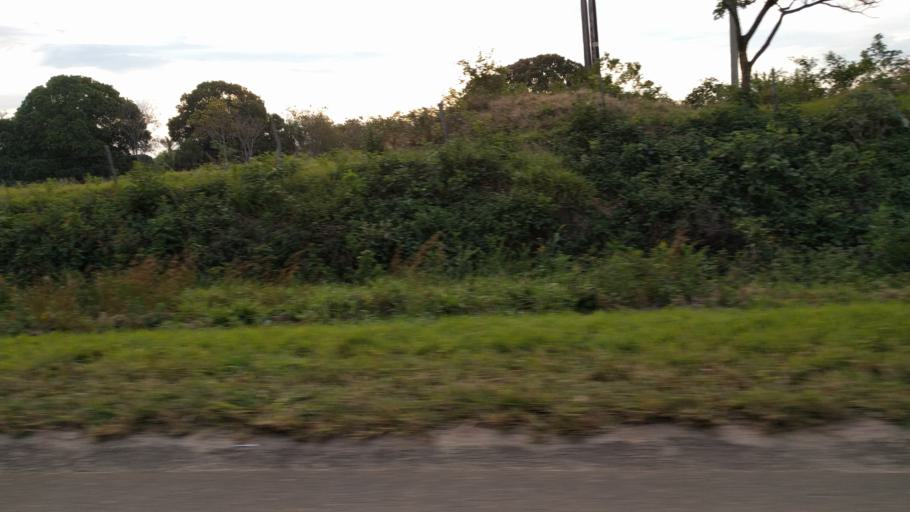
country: BO
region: Santa Cruz
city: Buena Vista
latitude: -17.4442
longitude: -63.6480
